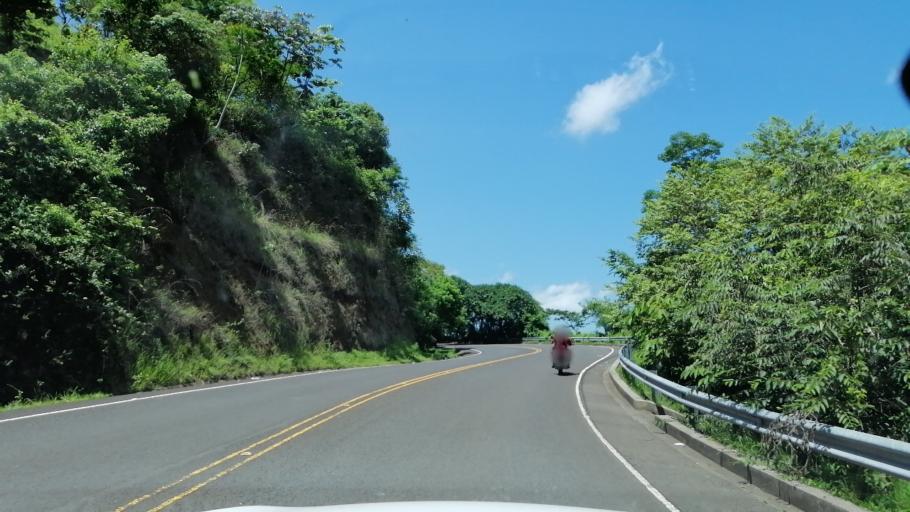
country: SV
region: San Miguel
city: Ciudad Barrios
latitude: 13.7948
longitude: -88.2910
